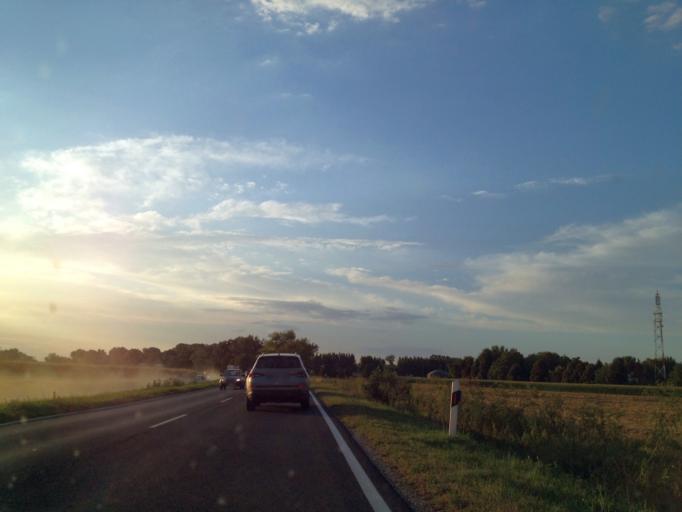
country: HU
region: Gyor-Moson-Sopron
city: Mosonmagyarovar
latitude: 47.8357
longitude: 17.2960
